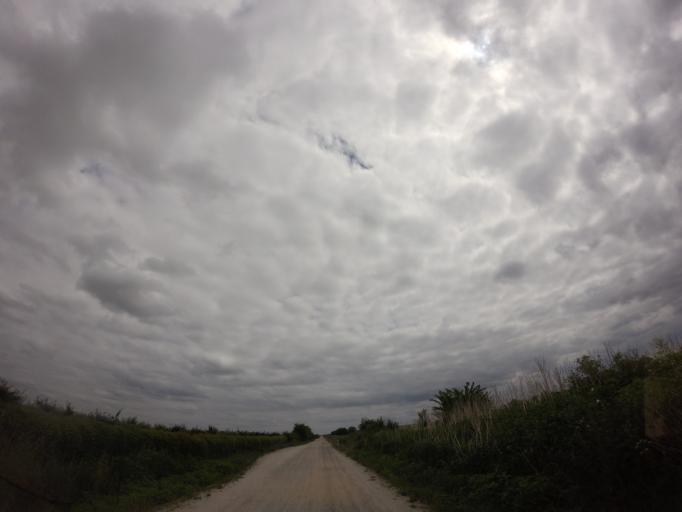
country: PL
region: Lubusz
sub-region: Powiat strzelecko-drezdenecki
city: Strzelce Krajenskie
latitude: 52.8827
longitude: 15.5568
